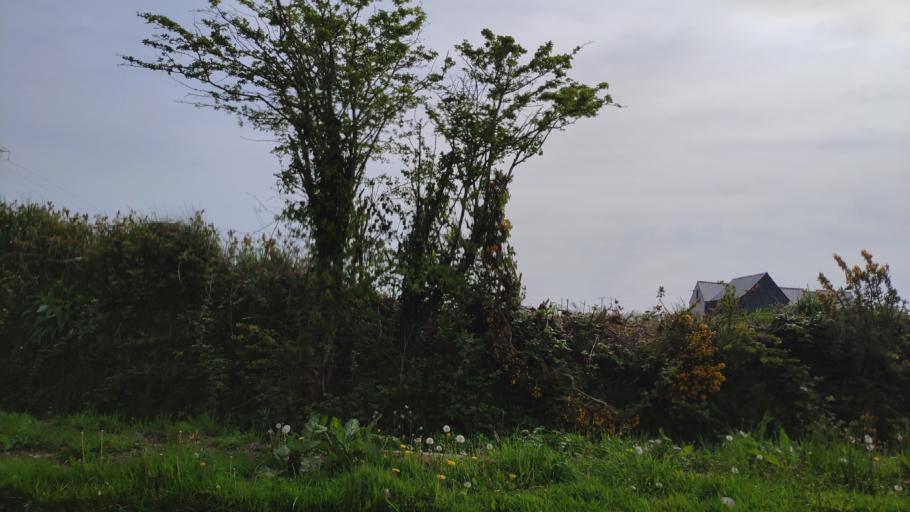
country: IE
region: Munster
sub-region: County Cork
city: Blarney
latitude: 51.9736
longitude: -8.5130
